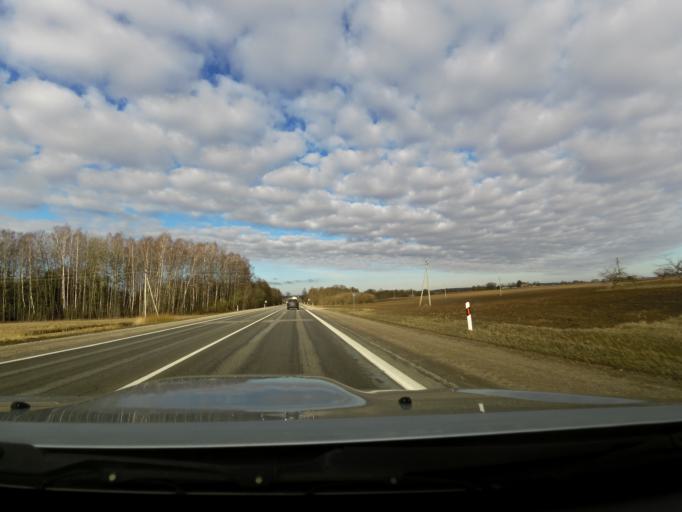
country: LT
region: Panevezys
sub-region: Panevezys City
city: Panevezys
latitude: 55.7528
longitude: 24.1313
